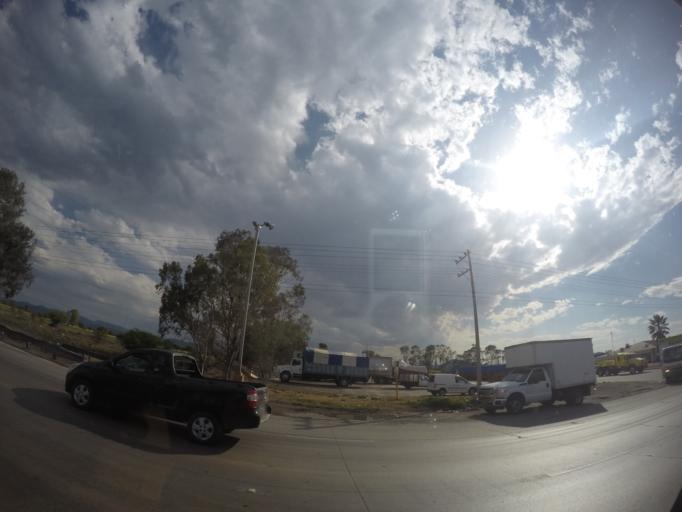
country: MX
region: Queretaro
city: El Sauz
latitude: 20.4814
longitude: -100.1137
